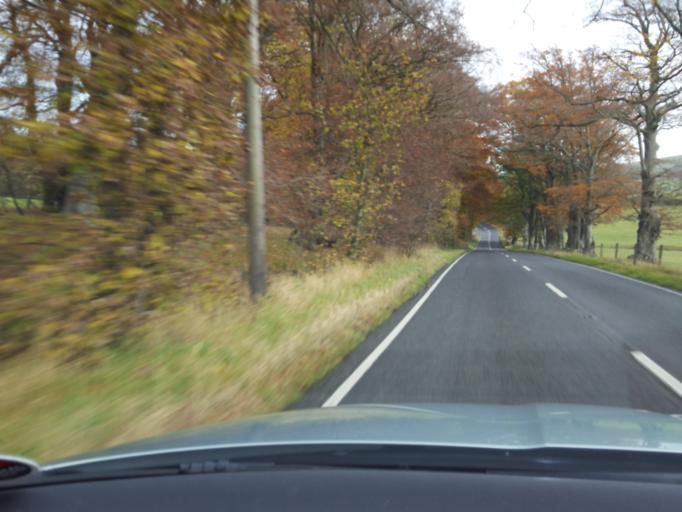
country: GB
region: Scotland
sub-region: The Scottish Borders
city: West Linton
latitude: 55.6847
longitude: -3.4174
